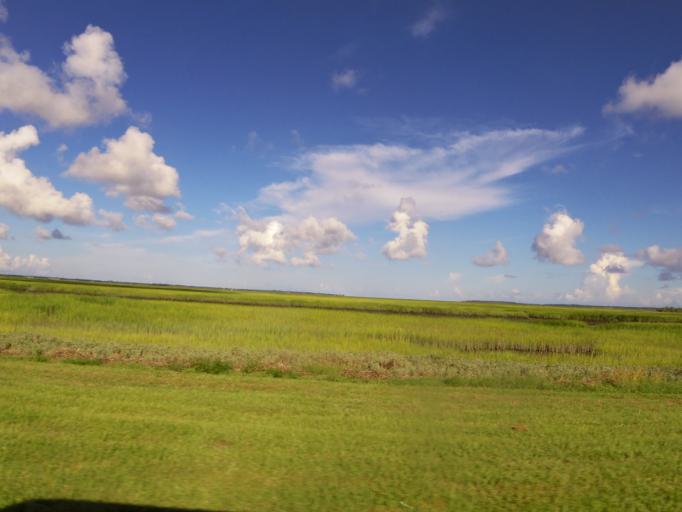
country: US
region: Georgia
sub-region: Glynn County
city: Brunswick
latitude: 31.1402
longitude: -81.4793
